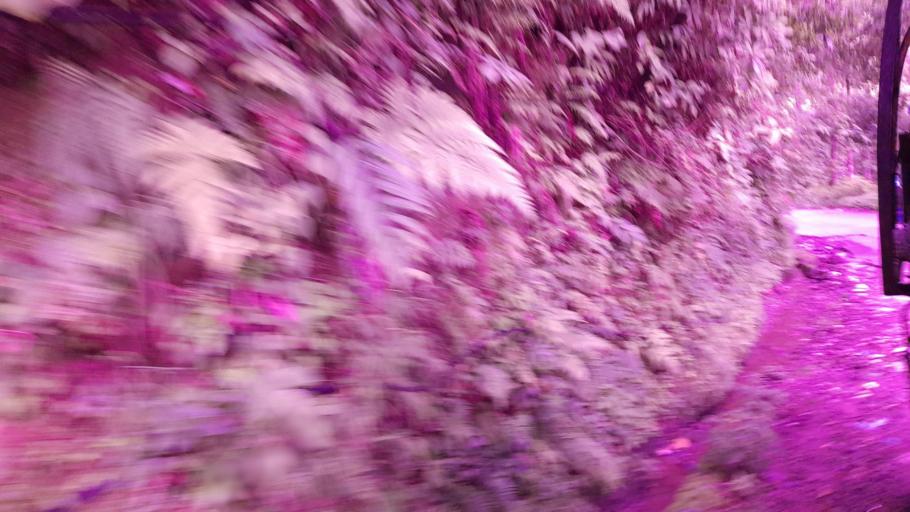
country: NP
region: Central Region
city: Kirtipur
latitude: 27.8296
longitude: 85.2092
